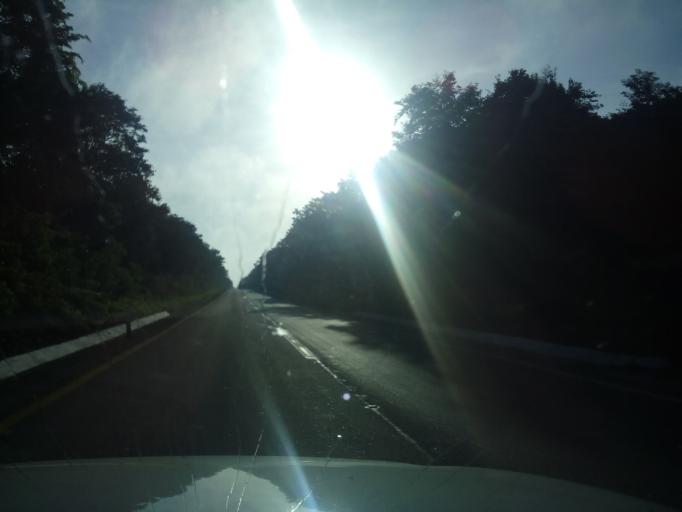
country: MX
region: Yucatan
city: Tunkas
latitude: 20.7595
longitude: -88.7712
